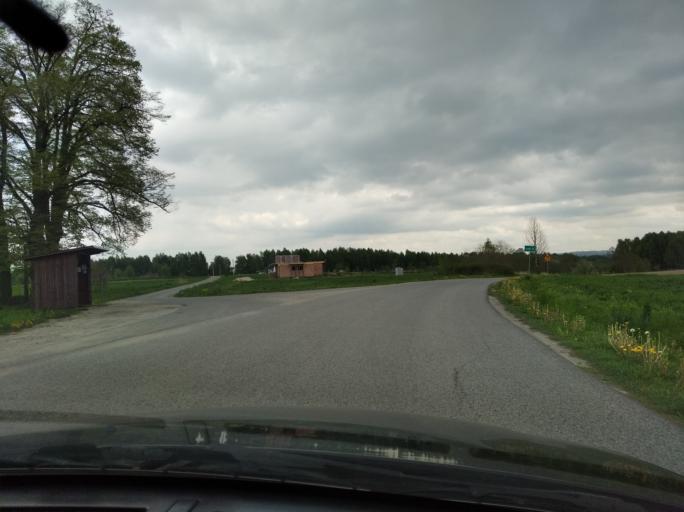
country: PL
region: Subcarpathian Voivodeship
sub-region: Powiat debicki
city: Leki Gorne
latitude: 49.9833
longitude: 21.1513
